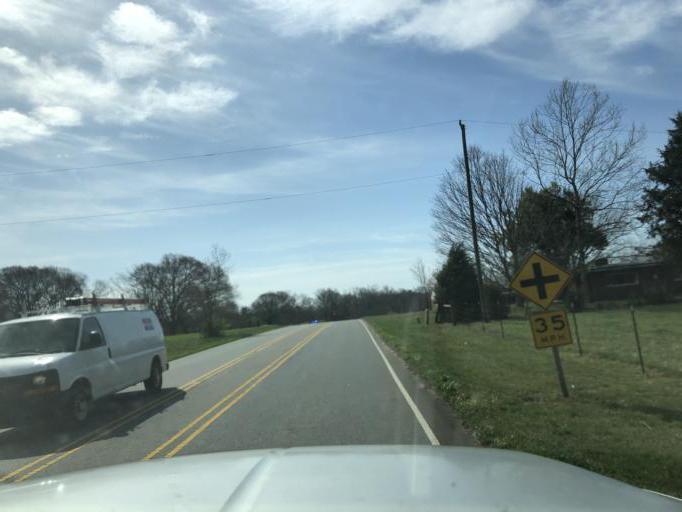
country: US
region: North Carolina
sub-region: Cleveland County
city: Shelby
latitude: 35.3890
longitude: -81.6236
